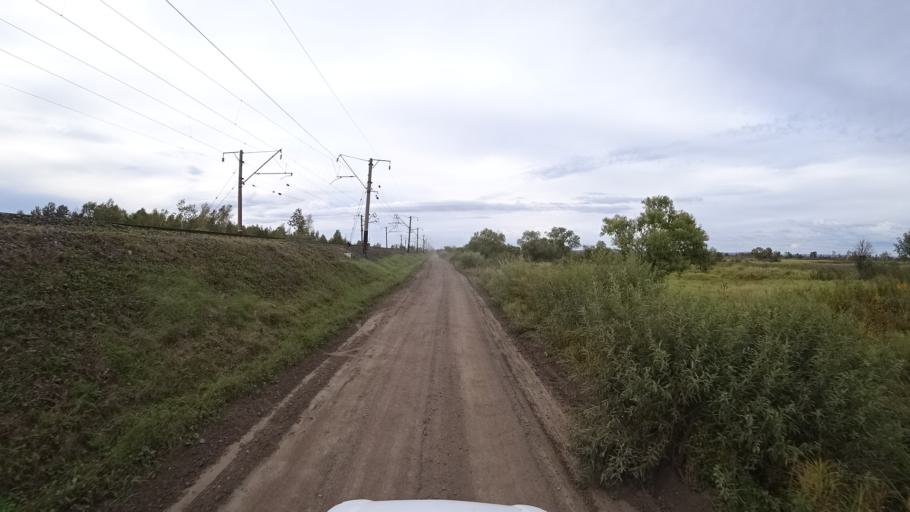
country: RU
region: Amur
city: Arkhara
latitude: 49.3556
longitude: 130.1544
